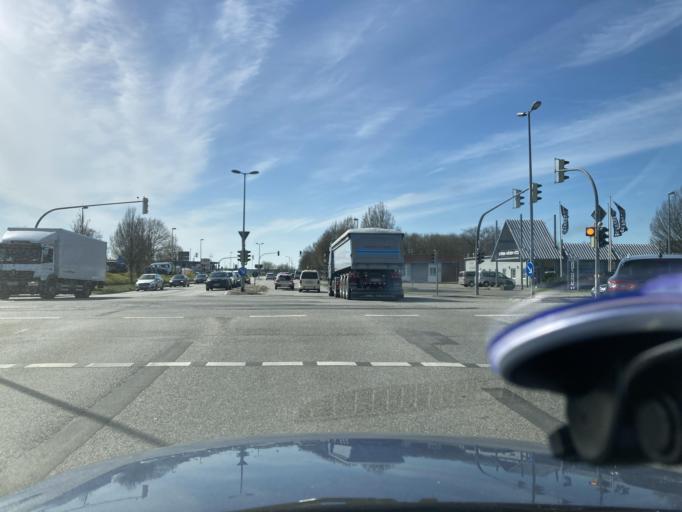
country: DE
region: Schleswig-Holstein
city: Heide
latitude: 54.1980
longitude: 9.1245
